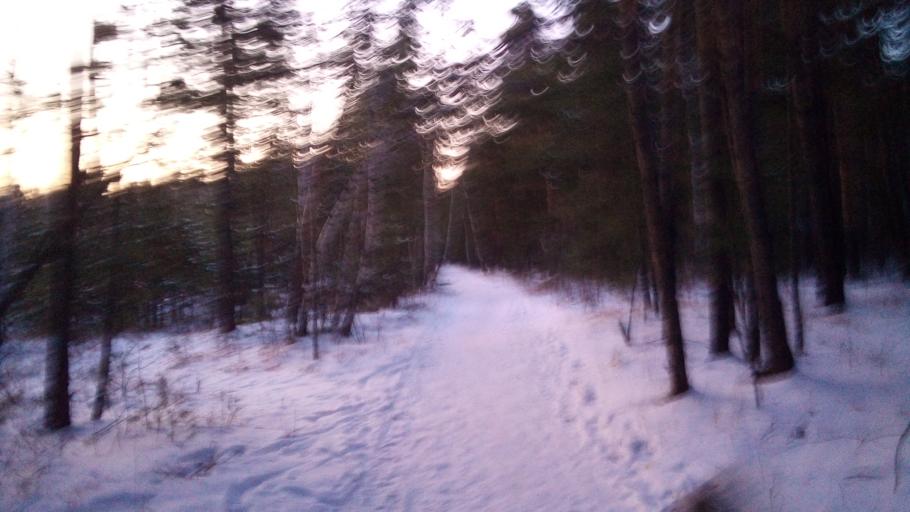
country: RU
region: Chelyabinsk
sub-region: Gorod Chelyabinsk
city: Chelyabinsk
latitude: 55.1604
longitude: 61.3330
